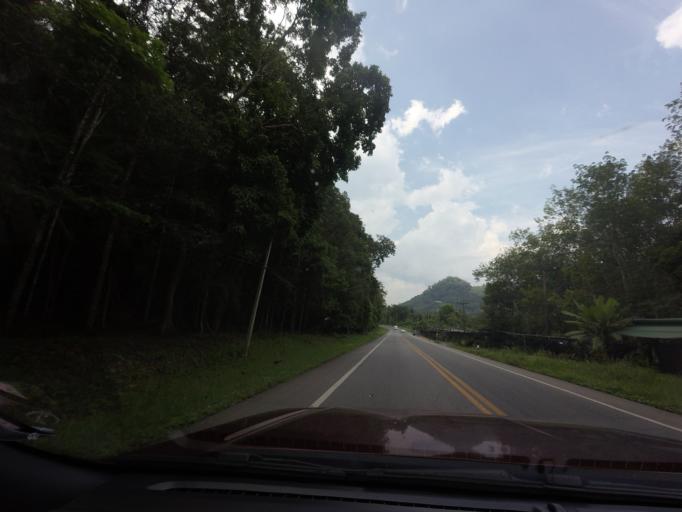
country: TH
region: Yala
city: Ban Nang Sata
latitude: 6.2369
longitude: 101.2168
